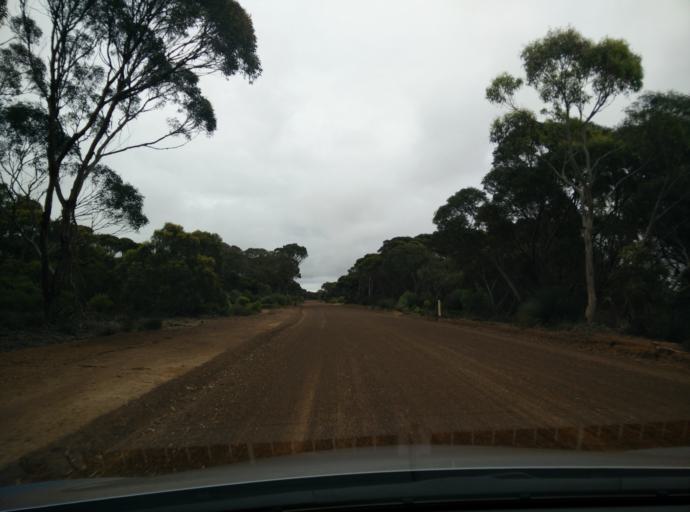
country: AU
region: South Australia
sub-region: Kangaroo Island
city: Kingscote
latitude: -35.8550
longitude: 137.4704
